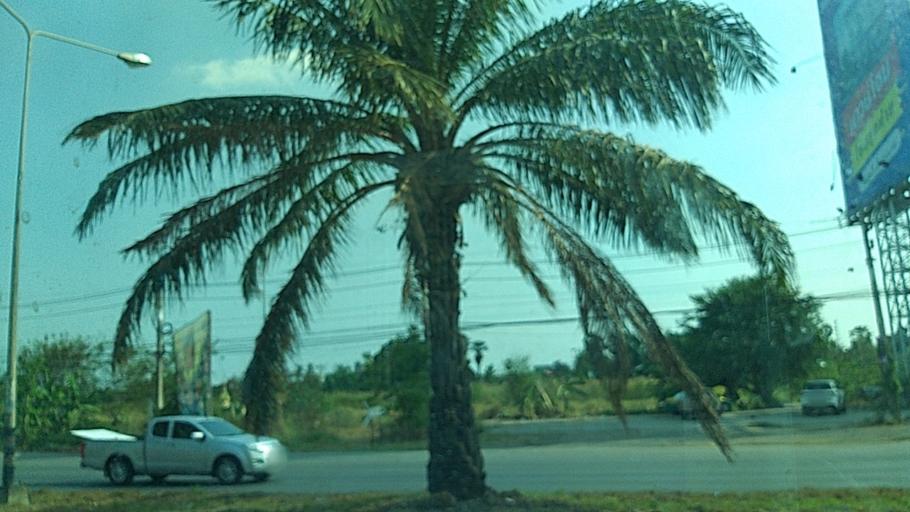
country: TH
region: Pathum Thani
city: Pathum Thani
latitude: 14.0295
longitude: 100.5350
